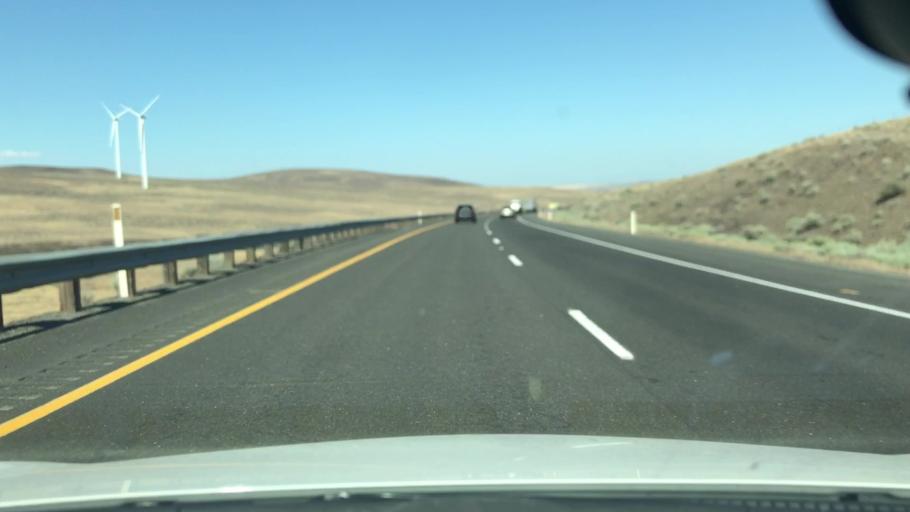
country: US
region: Washington
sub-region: Grant County
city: Mattawa
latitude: 46.9442
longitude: -120.1081
